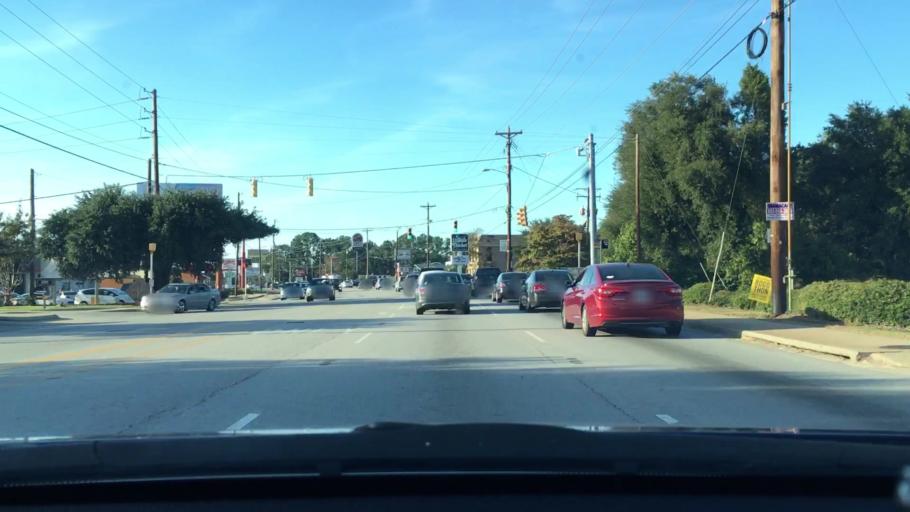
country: US
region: South Carolina
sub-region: Lexington County
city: Saint Andrews
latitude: 34.0351
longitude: -81.0891
